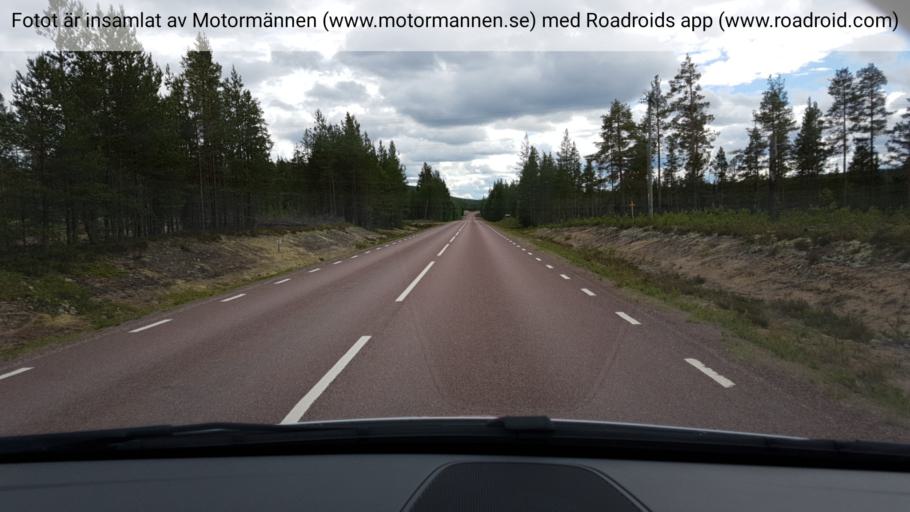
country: SE
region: Jaemtland
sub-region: Harjedalens Kommun
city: Sveg
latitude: 61.9155
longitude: 14.1782
